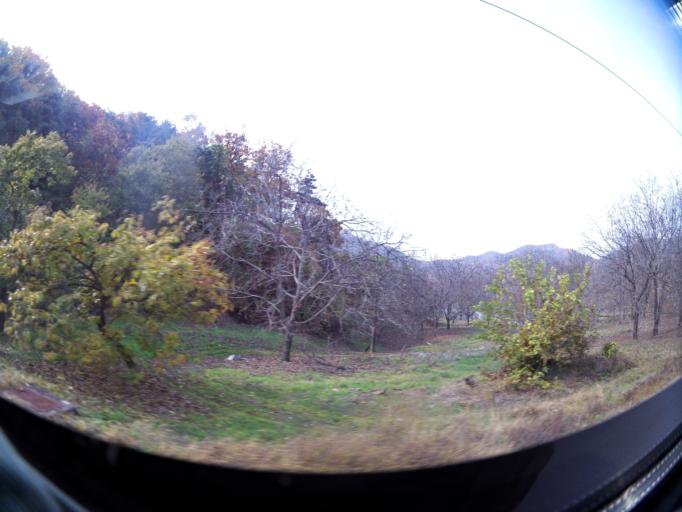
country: KR
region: Gyeongsangbuk-do
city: Gimcheon
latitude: 36.1500
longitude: 128.0118
